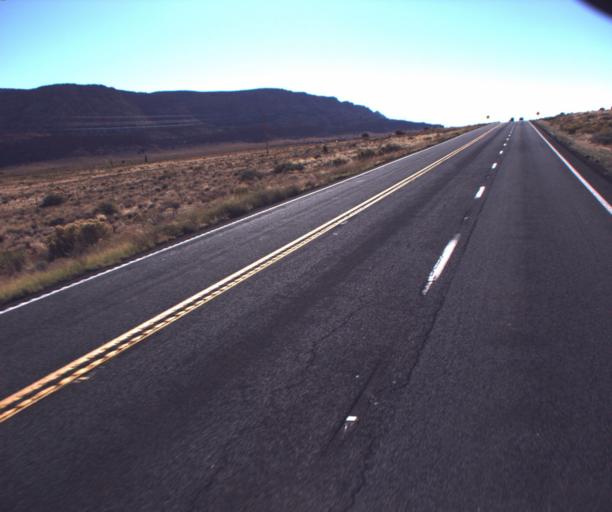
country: US
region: Arizona
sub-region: Coconino County
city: LeChee
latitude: 36.4465
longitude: -111.5576
